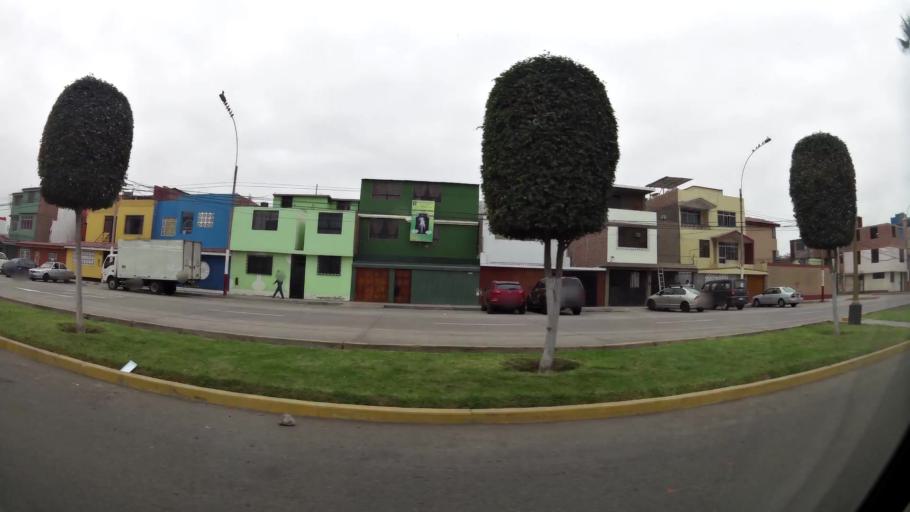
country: PE
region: Callao
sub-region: Callao
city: Callao
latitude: -12.0543
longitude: -77.1075
